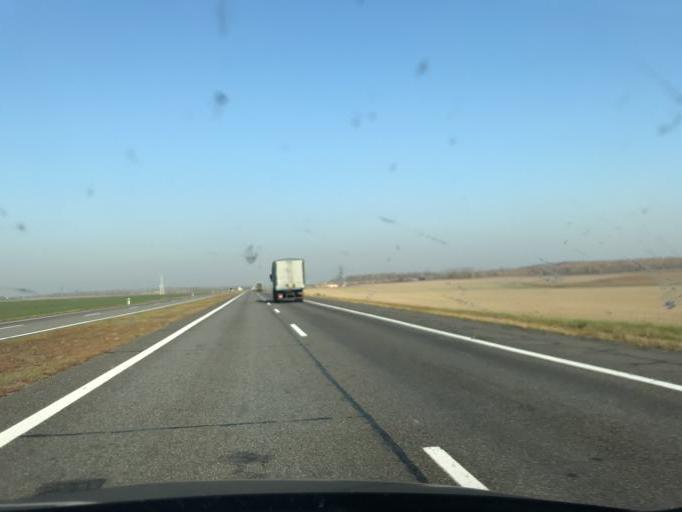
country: BY
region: Brest
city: Baranovichi
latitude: 53.2242
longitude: 26.1582
